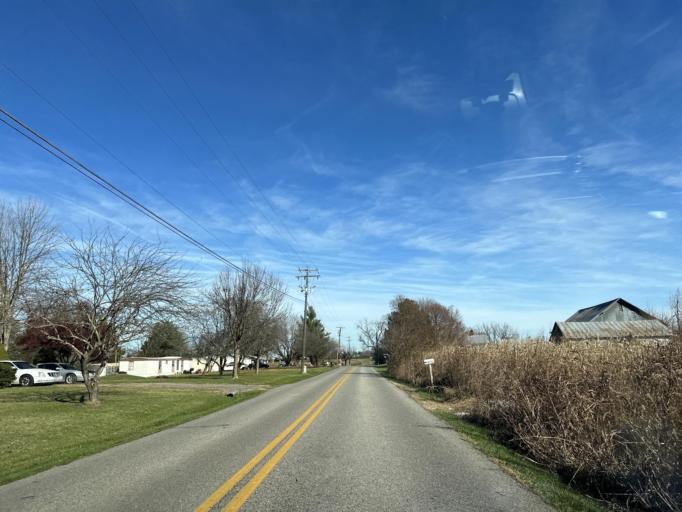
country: US
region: Virginia
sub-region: Augusta County
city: Crimora
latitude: 38.2109
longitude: -78.9016
